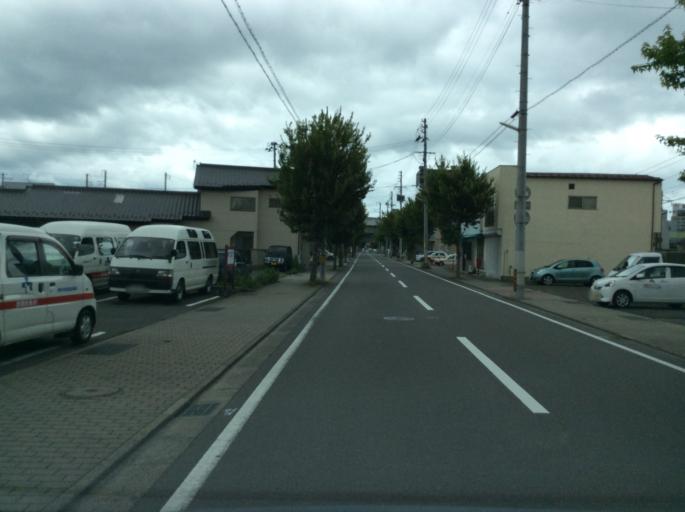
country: JP
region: Fukushima
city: Fukushima-shi
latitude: 37.7647
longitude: 140.4569
